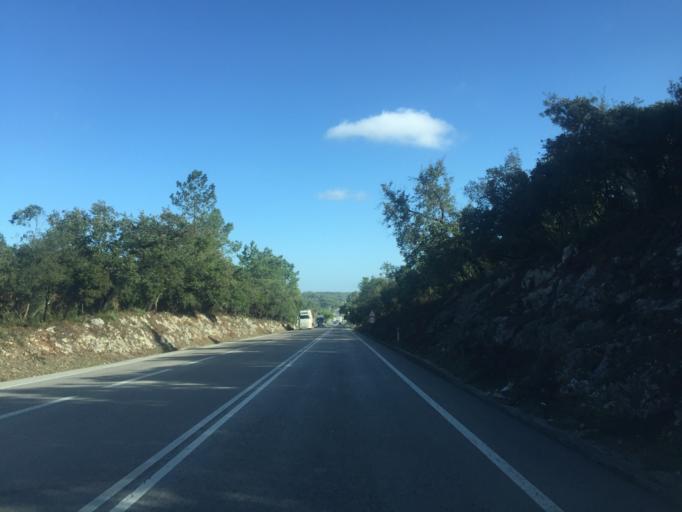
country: PT
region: Leiria
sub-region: Alcobaca
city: Aljubarrota
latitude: 39.5746
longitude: -8.8757
